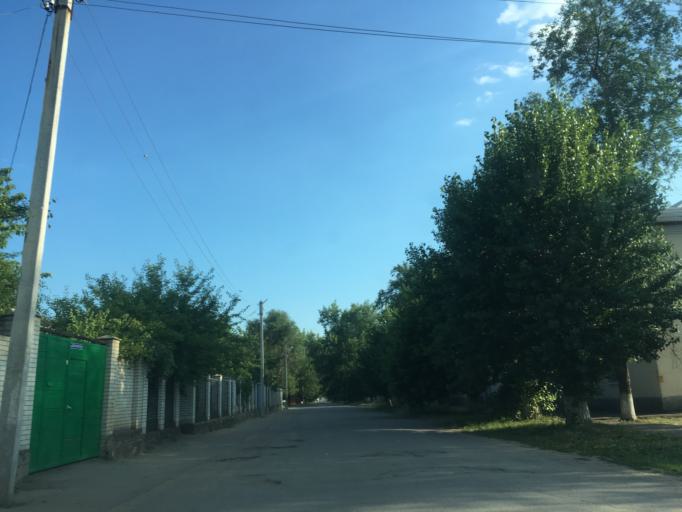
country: RU
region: Rostov
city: Masalovka
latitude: 48.4042
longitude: 40.2786
